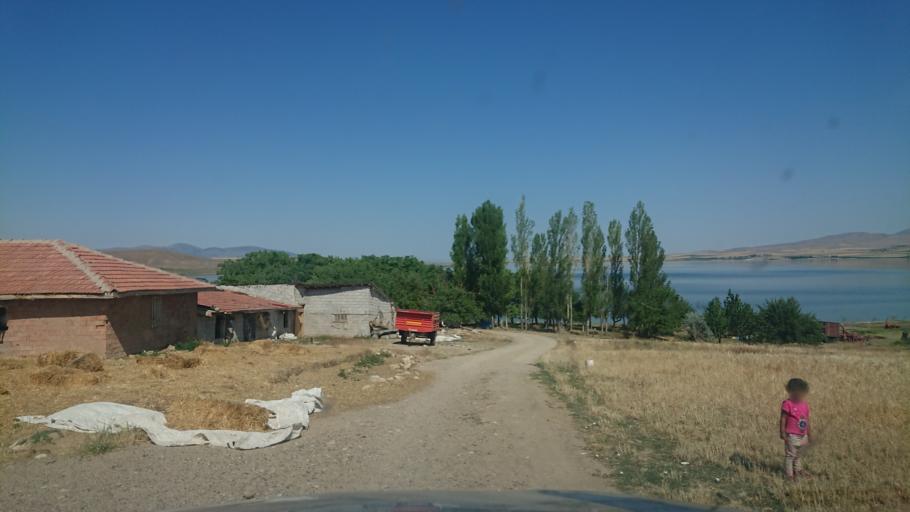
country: TR
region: Ankara
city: Evren
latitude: 39.0513
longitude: 33.8774
